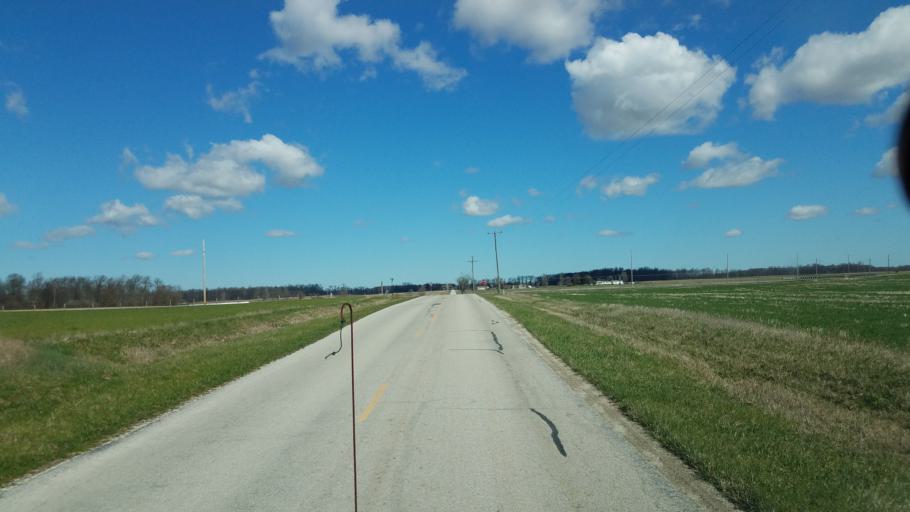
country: US
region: Ohio
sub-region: Sandusky County
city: Mount Carmel
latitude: 41.2052
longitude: -82.9373
